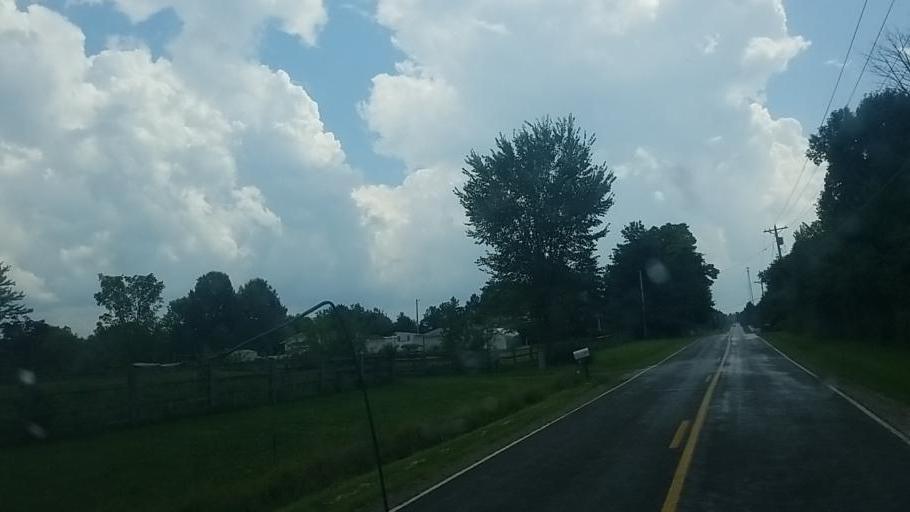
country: US
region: Ohio
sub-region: Lorain County
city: Grafton
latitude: 41.1791
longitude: -82.0036
